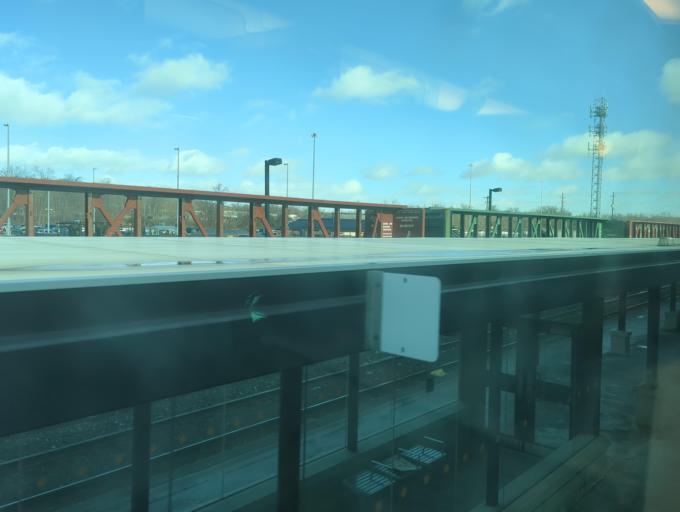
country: CA
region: Ontario
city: Hamilton
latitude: 43.3124
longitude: -79.8559
